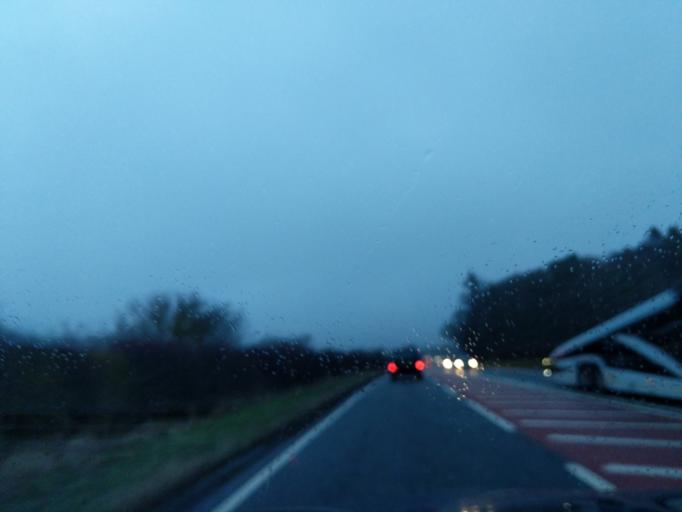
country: GB
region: England
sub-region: Northumberland
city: Felton
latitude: 55.2610
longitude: -1.7084
